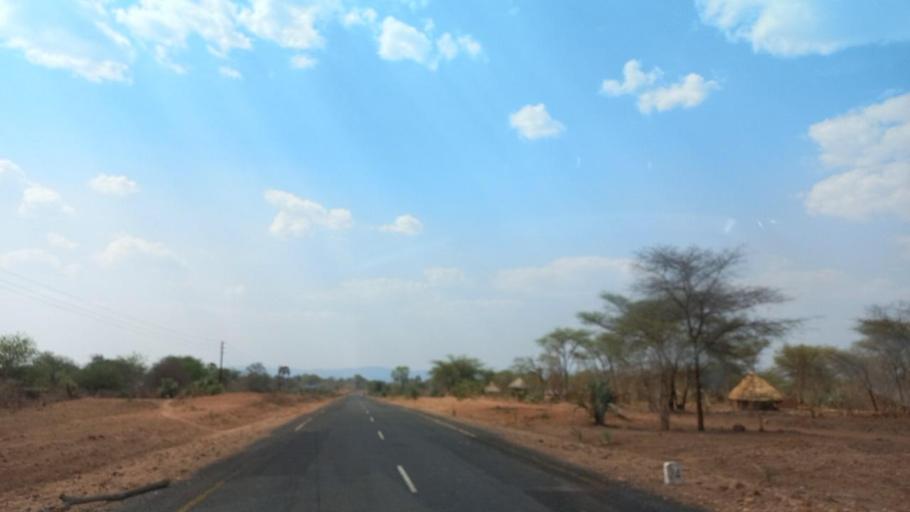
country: ZM
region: Lusaka
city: Luangwa
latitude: -15.1638
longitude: 30.2120
